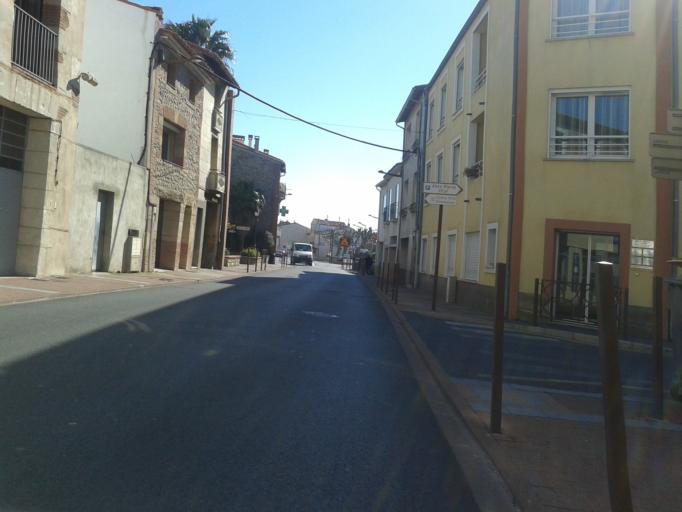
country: FR
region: Languedoc-Roussillon
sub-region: Departement des Pyrenees-Orientales
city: Le Soler
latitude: 42.6816
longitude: 2.7943
